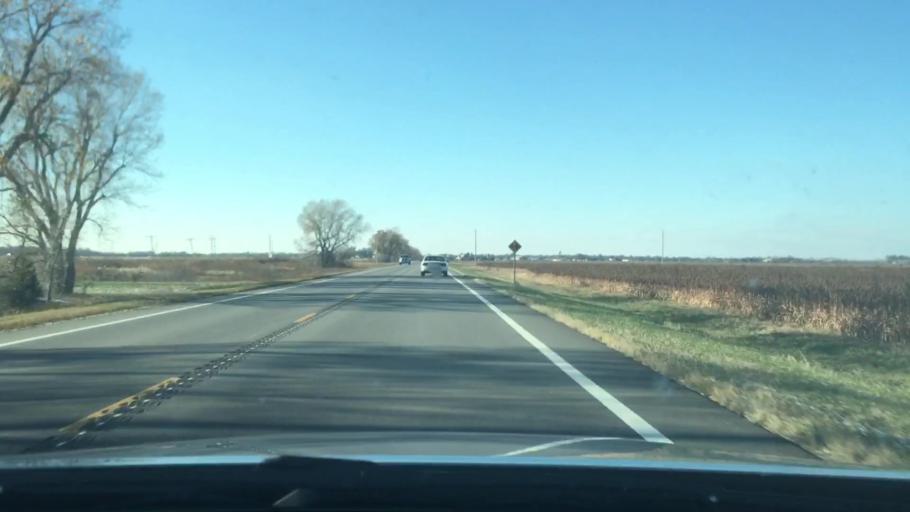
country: US
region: Kansas
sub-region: Reno County
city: Nickerson
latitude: 38.1284
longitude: -98.0559
